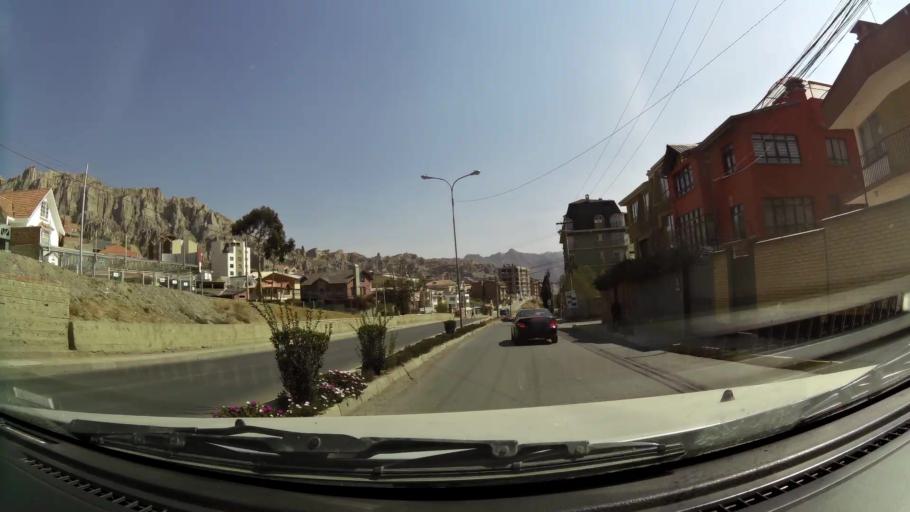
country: BO
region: La Paz
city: La Paz
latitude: -16.5455
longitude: -68.0729
